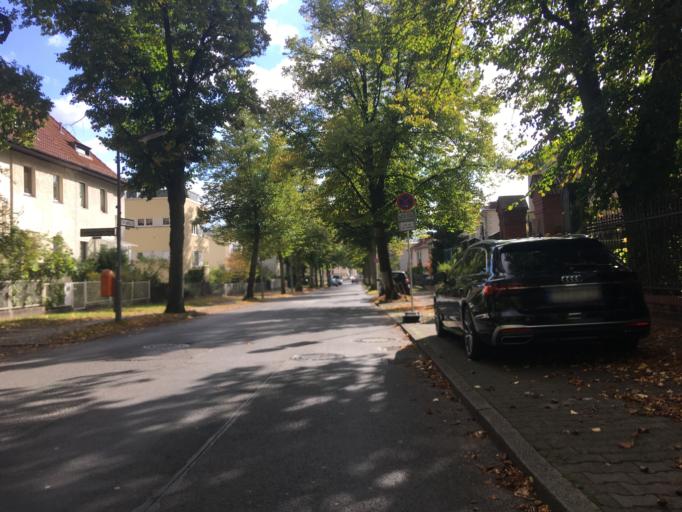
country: DE
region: Berlin
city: Lankwitz
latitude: 52.4458
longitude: 13.3537
